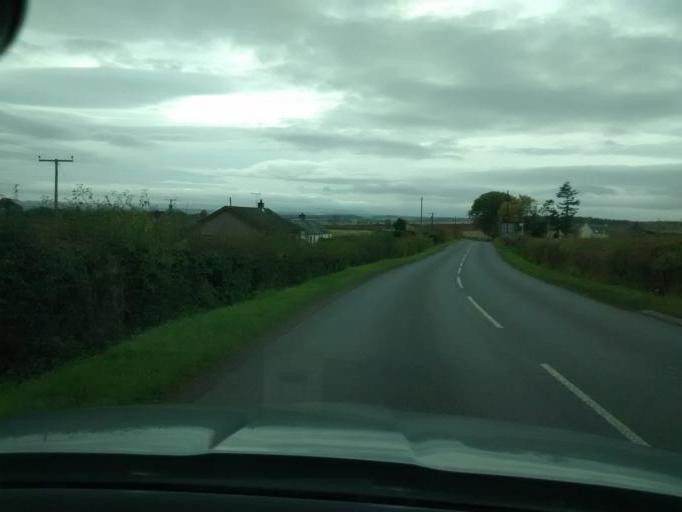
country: GB
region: Scotland
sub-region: Perth and Kinross
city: Stanley
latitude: 56.4920
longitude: -3.4499
